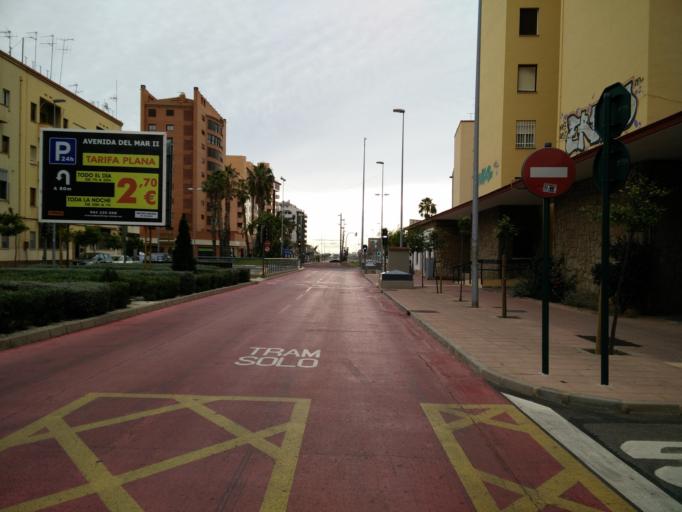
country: ES
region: Valencia
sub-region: Provincia de Castello
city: Castello de la Plana
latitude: 39.9846
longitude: -0.0293
